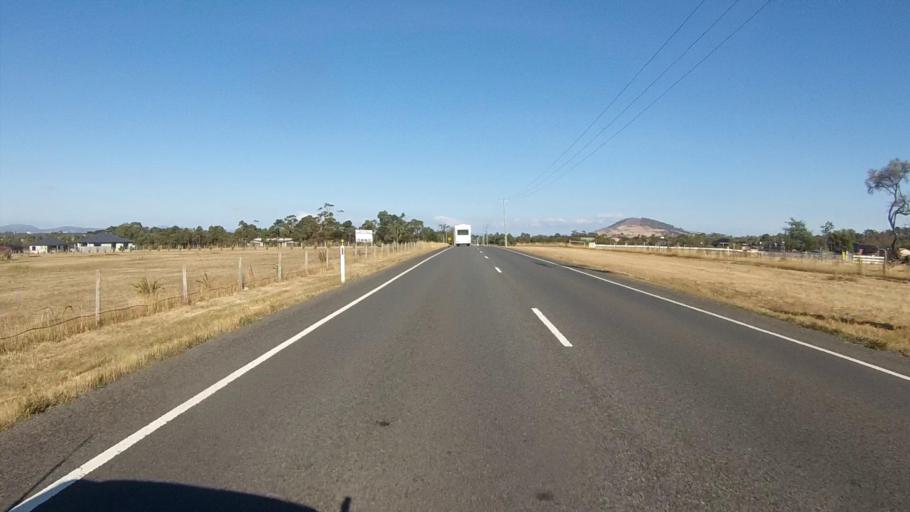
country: AU
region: Tasmania
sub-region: Clarence
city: Cambridge
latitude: -42.8410
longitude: 147.4698
